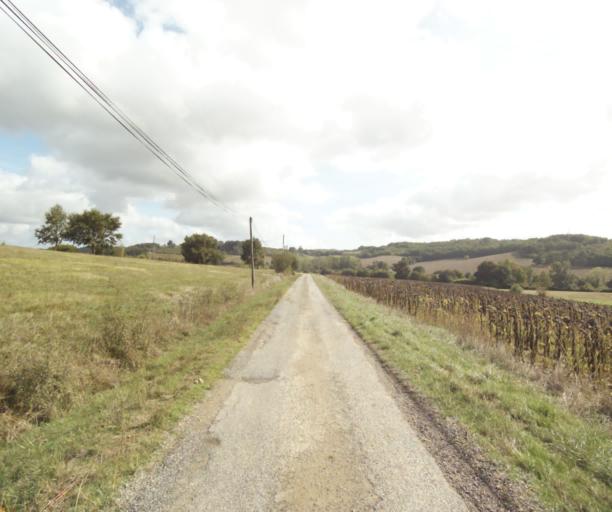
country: FR
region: Midi-Pyrenees
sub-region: Departement du Tarn-et-Garonne
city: Beaumont-de-Lomagne
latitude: 43.8614
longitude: 1.0970
